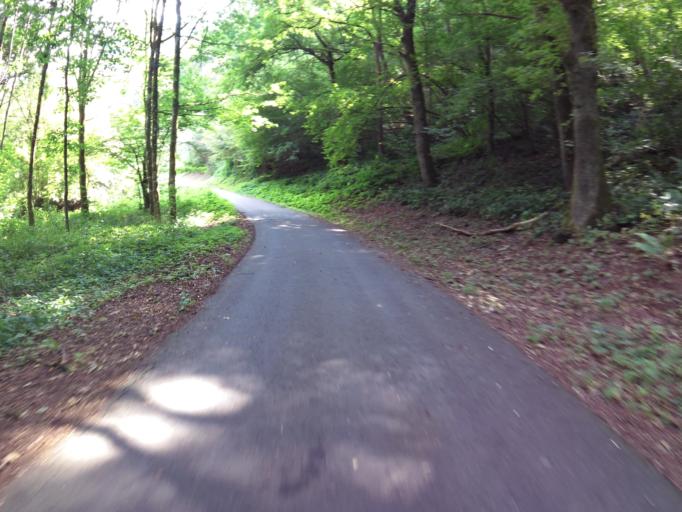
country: DE
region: Rheinland-Pfalz
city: Kordel
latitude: 49.8224
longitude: 6.6452
